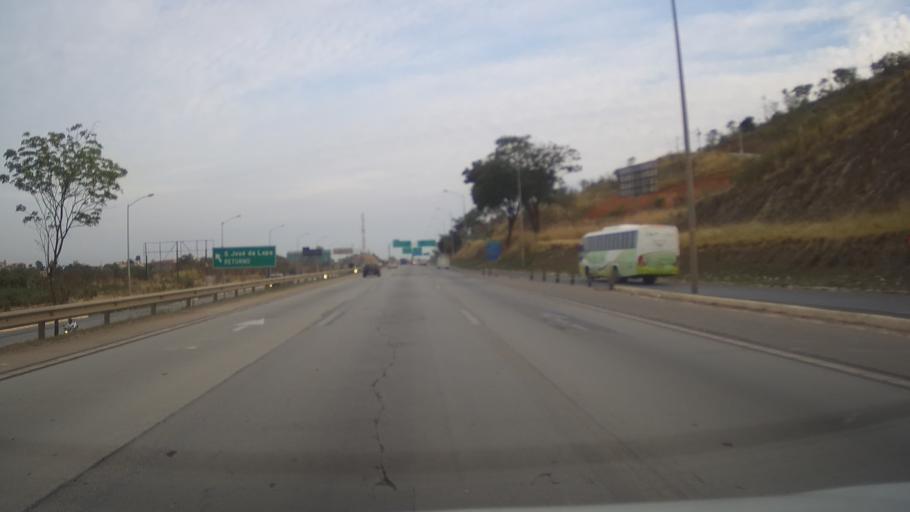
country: BR
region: Minas Gerais
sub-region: Vespasiano
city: Vespasiano
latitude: -19.7676
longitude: -43.9482
